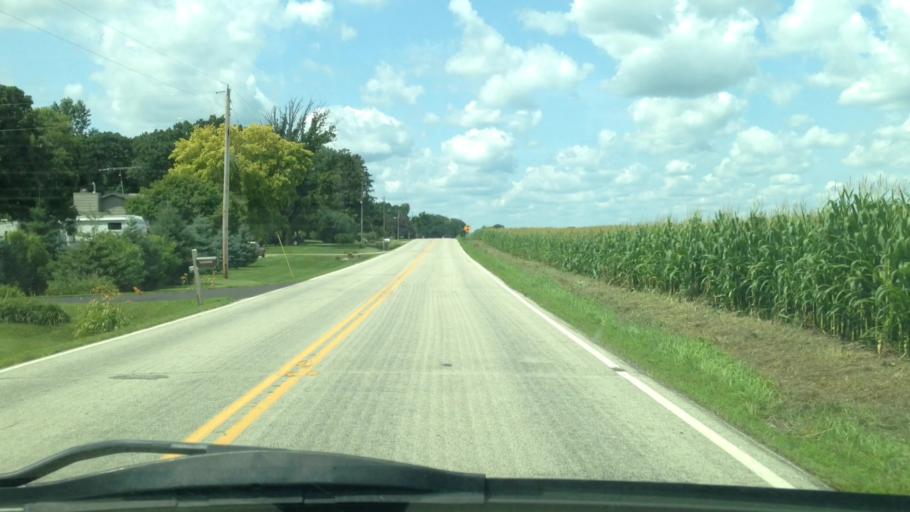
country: US
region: Minnesota
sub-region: Olmsted County
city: Rochester
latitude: 43.9532
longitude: -92.5139
